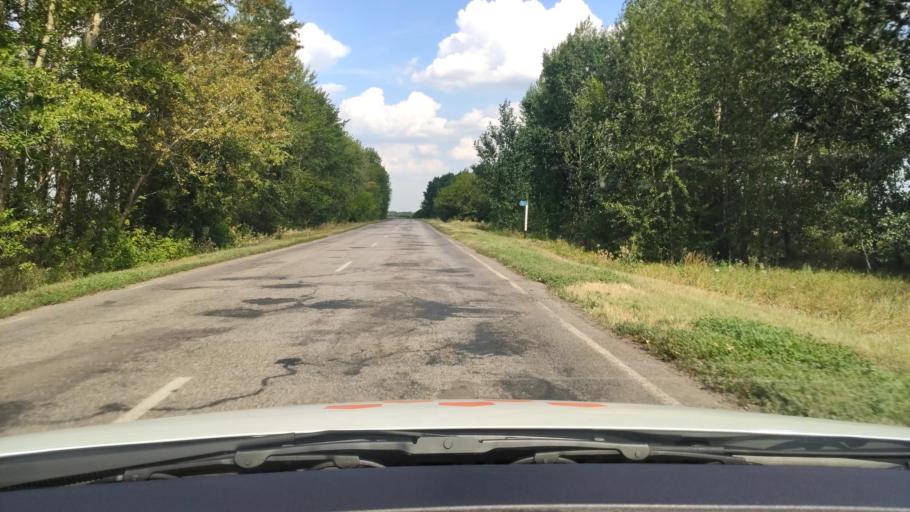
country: RU
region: Voronezj
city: Pereleshinskiy
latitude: 51.7233
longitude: 40.3633
